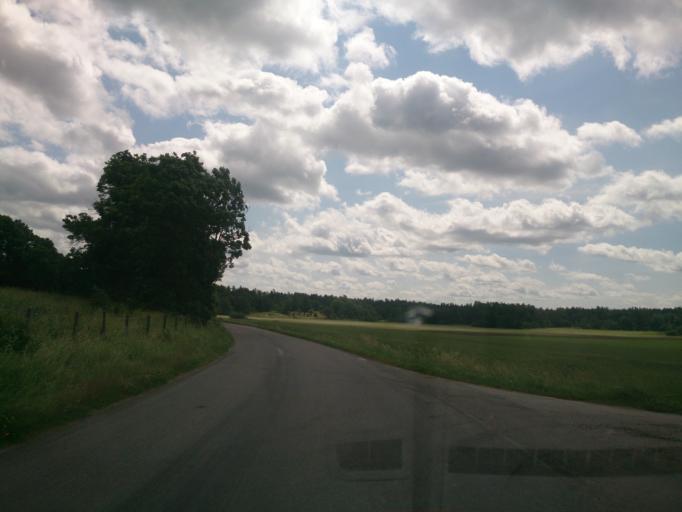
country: SE
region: OEstergoetland
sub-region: Norrkopings Kommun
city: Krokek
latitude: 58.5098
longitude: 16.5314
